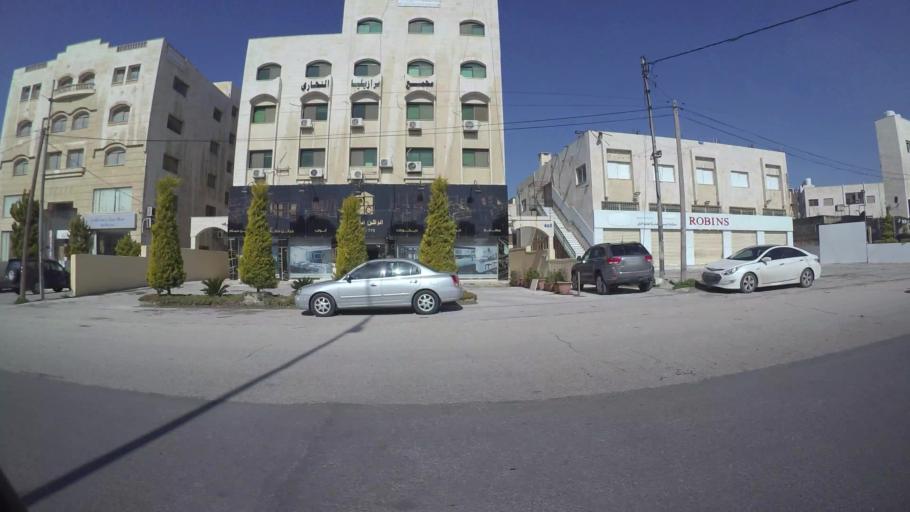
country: JO
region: Amman
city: Al Bunayyat ash Shamaliyah
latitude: 31.9086
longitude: 35.8889
